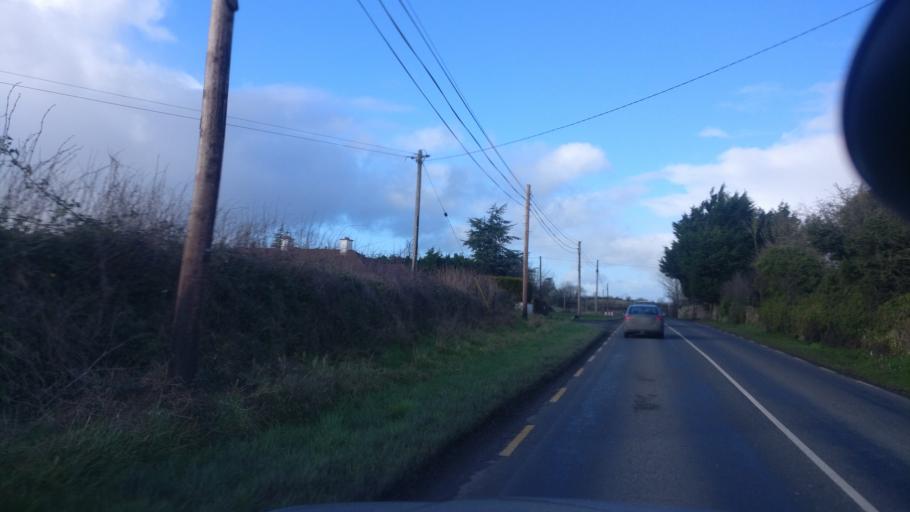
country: IE
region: Leinster
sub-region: Kilkenny
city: Kilkenny
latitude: 52.6284
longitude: -7.2169
